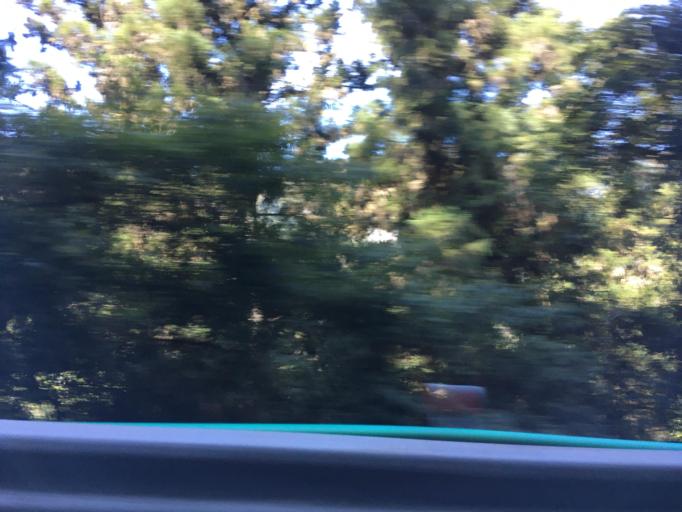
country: TW
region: Taiwan
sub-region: Yilan
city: Yilan
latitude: 24.5464
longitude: 121.5127
